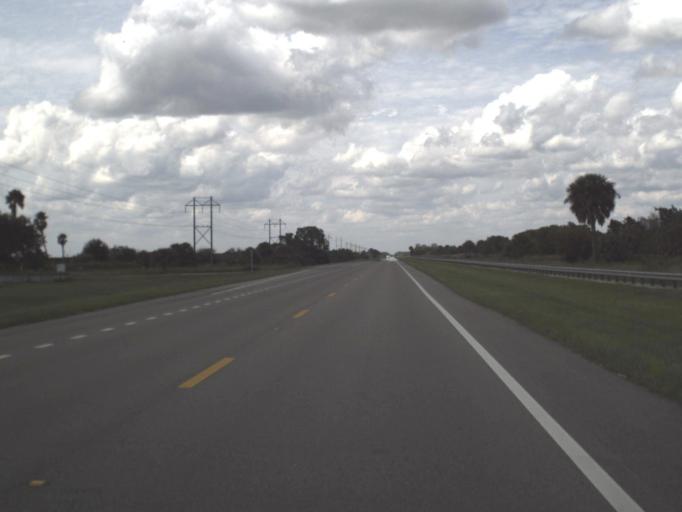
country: US
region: Florida
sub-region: Collier County
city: Immokalee
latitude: 26.3683
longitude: -81.3527
